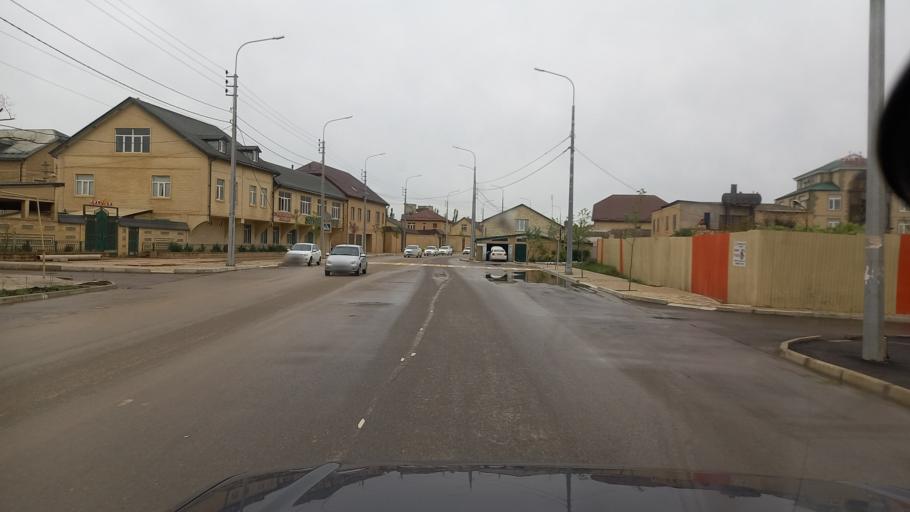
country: RU
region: Dagestan
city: Derbent
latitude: 42.0897
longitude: 48.2900
